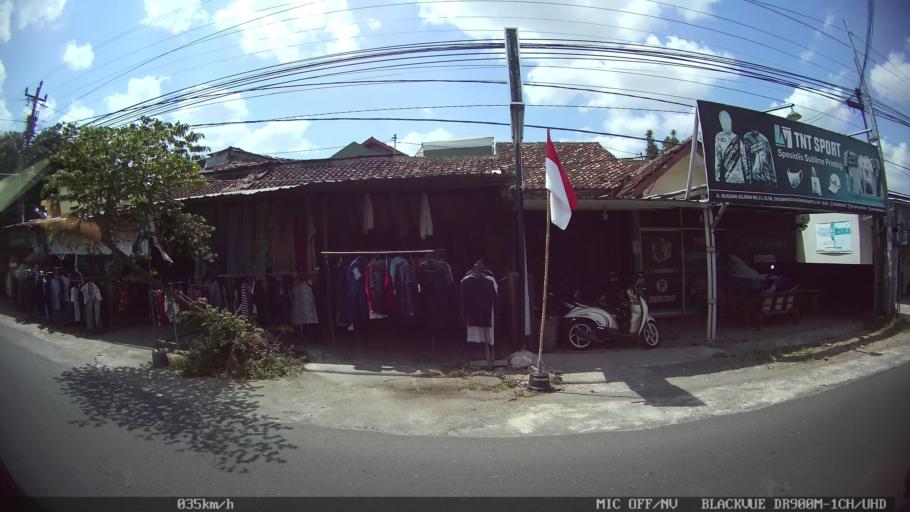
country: ID
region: Daerah Istimewa Yogyakarta
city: Kasihan
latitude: -7.8199
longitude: 110.3480
